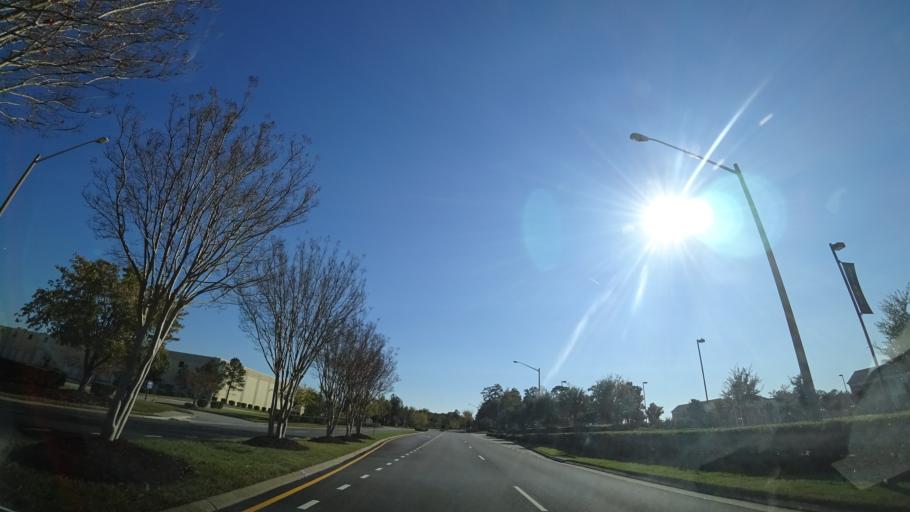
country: US
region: Virginia
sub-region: City of Newport News
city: Newport News
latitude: 36.8862
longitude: -76.4373
